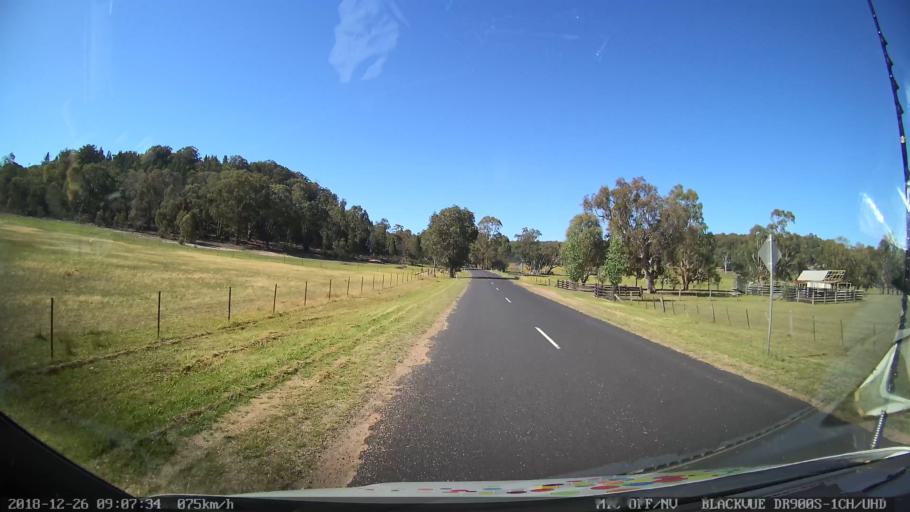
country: AU
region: New South Wales
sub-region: Mid-Western Regional
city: Kandos
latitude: -32.7070
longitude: 150.0038
